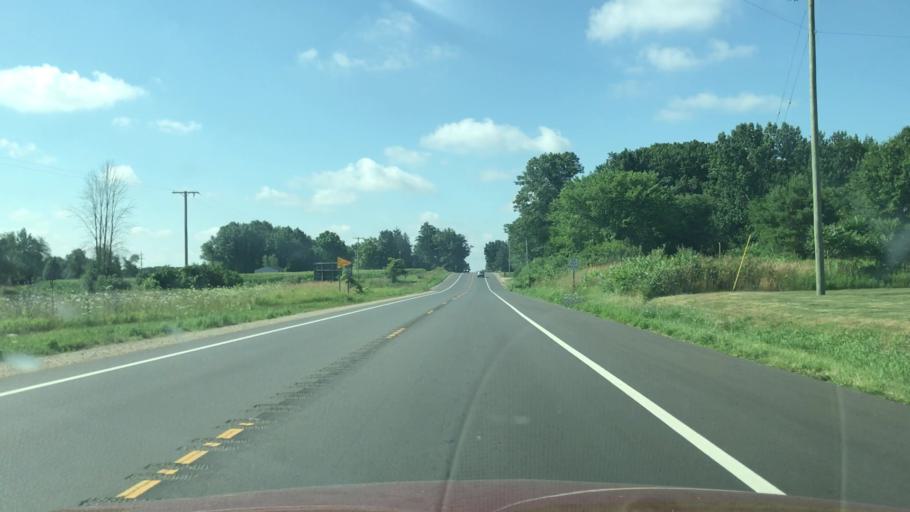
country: US
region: Michigan
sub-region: Newaygo County
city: Newaygo
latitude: 43.3747
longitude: -85.8009
